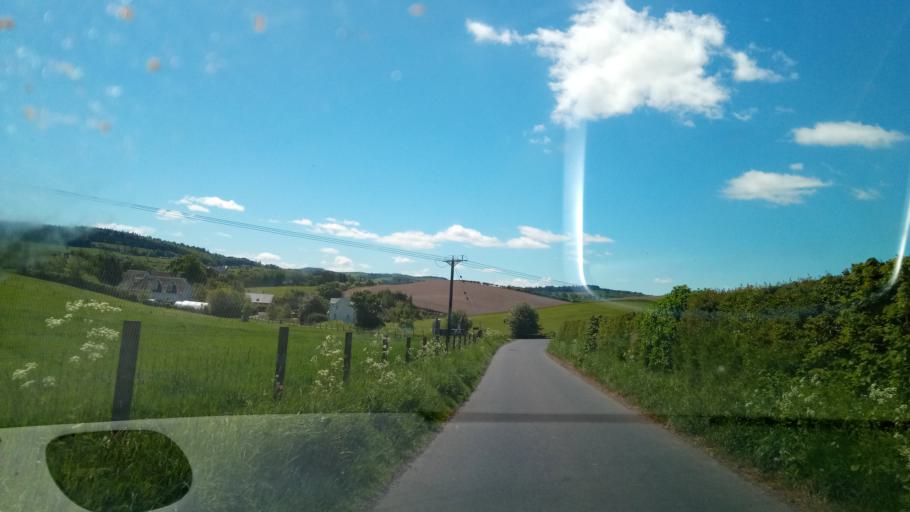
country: GB
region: Scotland
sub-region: The Scottish Borders
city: Hawick
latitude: 55.4508
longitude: -2.7367
